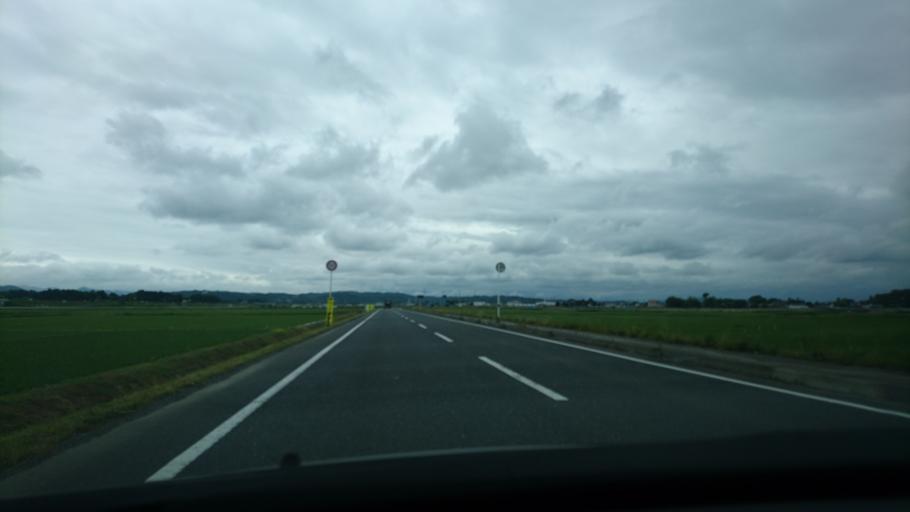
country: JP
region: Miyagi
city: Wakuya
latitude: 38.6821
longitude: 141.2611
